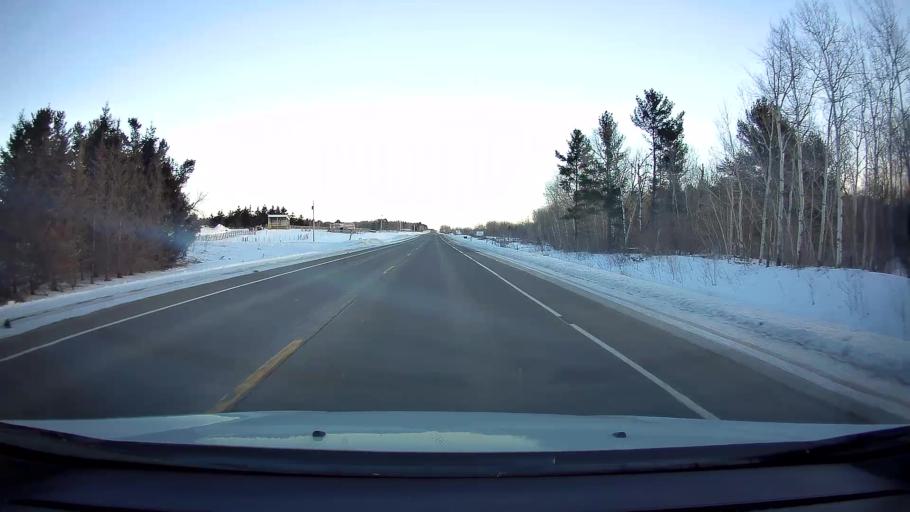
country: US
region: Wisconsin
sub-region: Barron County
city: Cumberland
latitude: 45.6129
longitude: -92.0083
